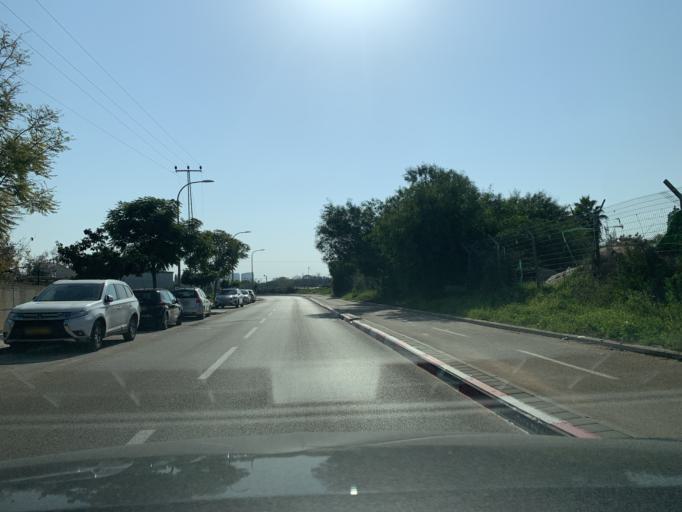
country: IL
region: Central District
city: Hod HaSharon
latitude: 32.1528
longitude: 34.8980
